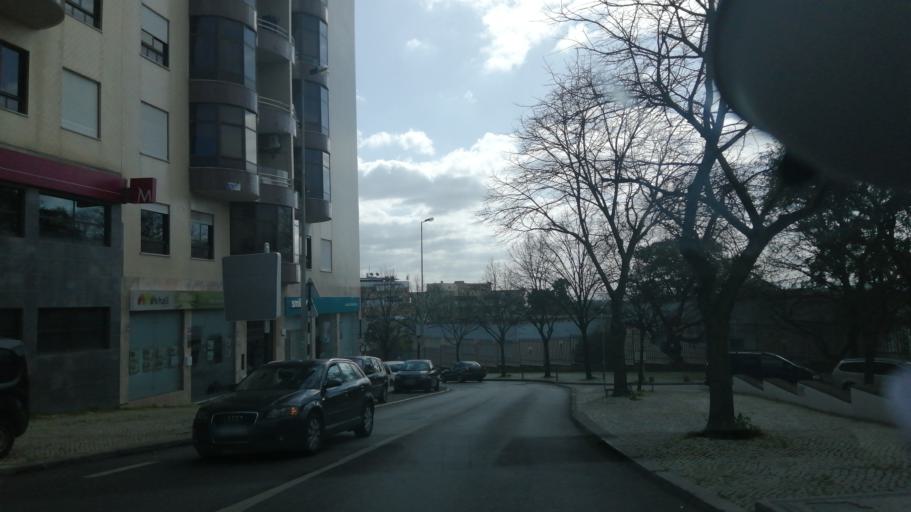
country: PT
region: Setubal
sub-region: Almada
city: Pragal
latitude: 38.6759
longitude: -9.1646
